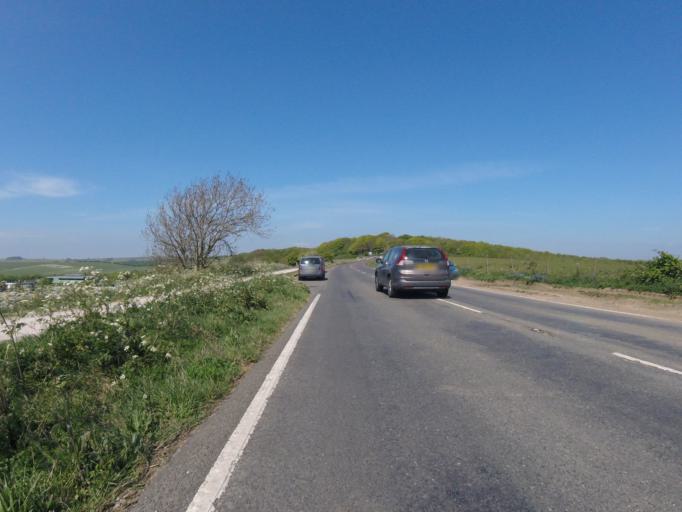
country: GB
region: England
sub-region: Brighton and Hove
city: Brighton
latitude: 50.8662
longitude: -0.1202
